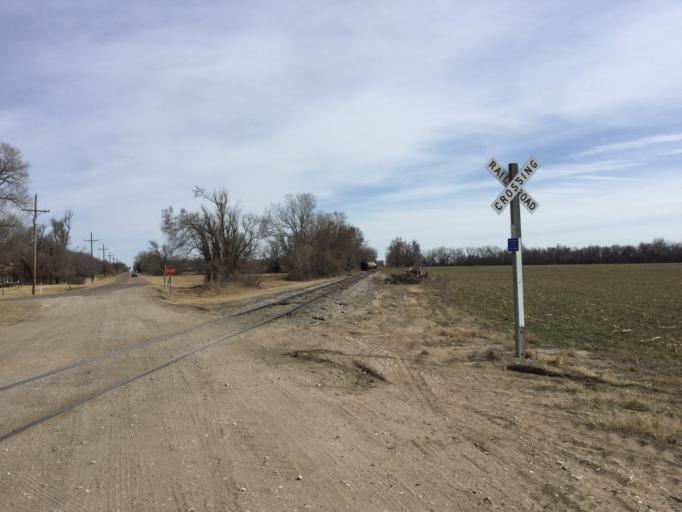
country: US
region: Kansas
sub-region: Rice County
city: Sterling
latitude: 38.2462
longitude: -98.3243
